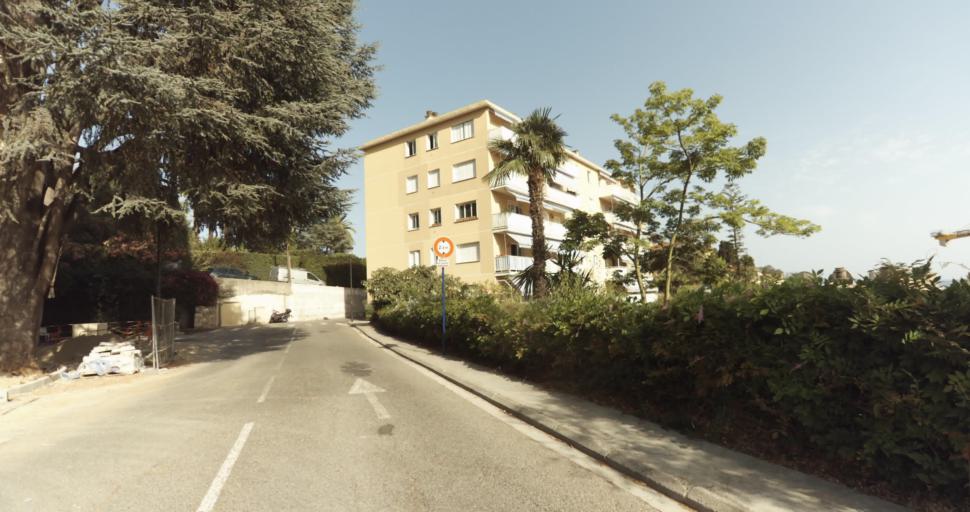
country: FR
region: Provence-Alpes-Cote d'Azur
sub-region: Departement des Alpes-Maritimes
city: Roquebrune-Cap-Martin
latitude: 43.7769
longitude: 7.4894
